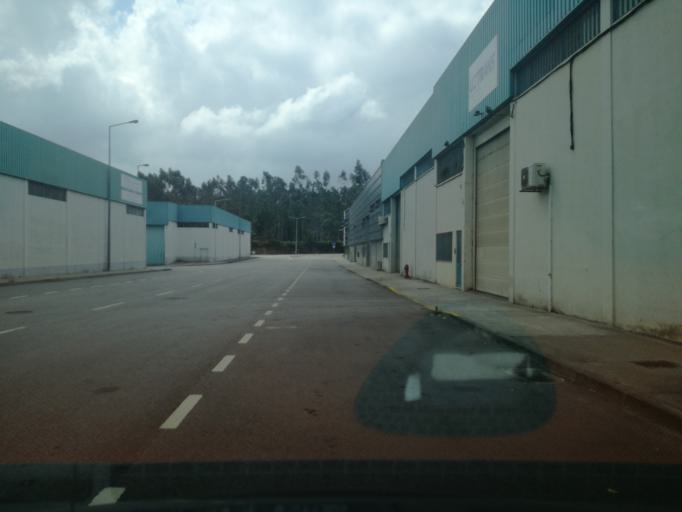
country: PT
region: Porto
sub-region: Maia
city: Anta
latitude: 41.2580
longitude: -8.6323
